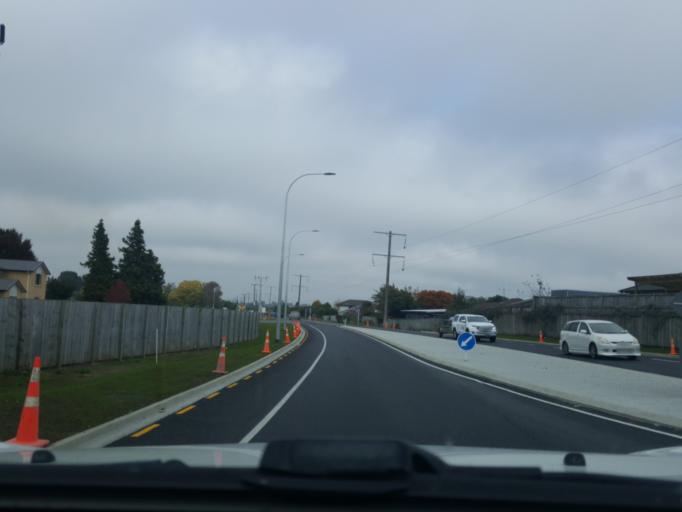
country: NZ
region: Waikato
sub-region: Hamilton City
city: Hamilton
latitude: -37.7324
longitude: 175.2873
